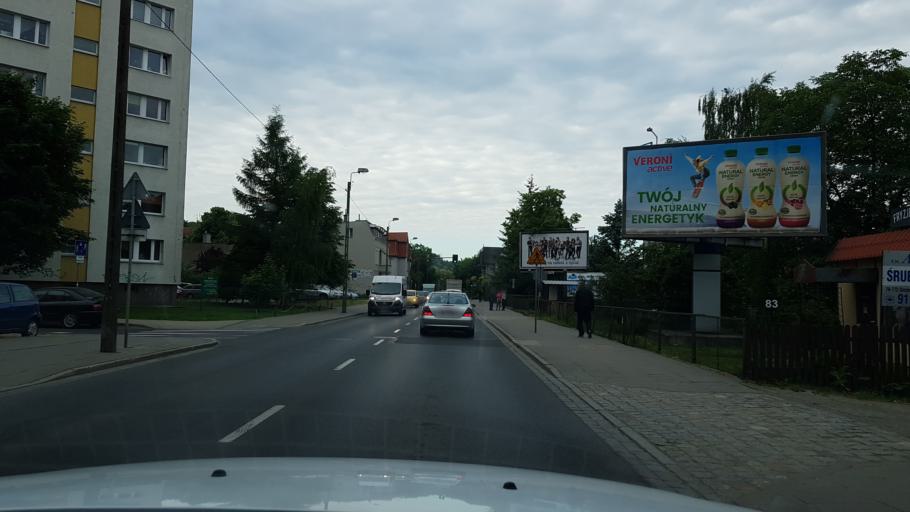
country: PL
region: West Pomeranian Voivodeship
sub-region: Szczecin
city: Szczecin
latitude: 53.3820
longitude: 14.6314
